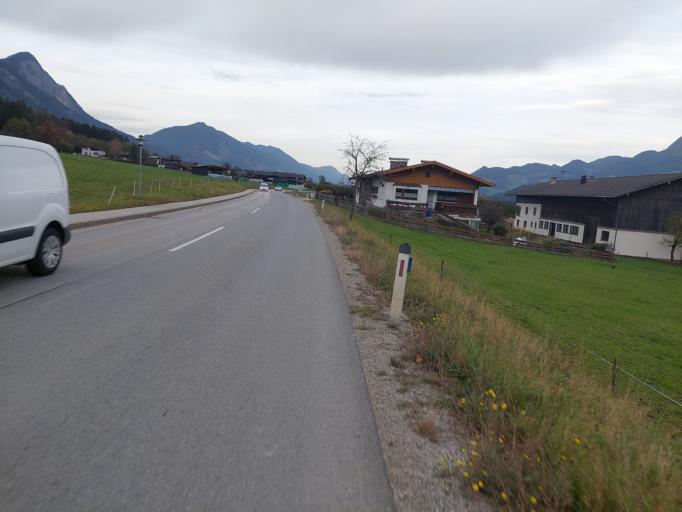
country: AT
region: Tyrol
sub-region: Politischer Bezirk Schwaz
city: Strass im Zillertal
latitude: 47.4068
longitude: 11.8225
